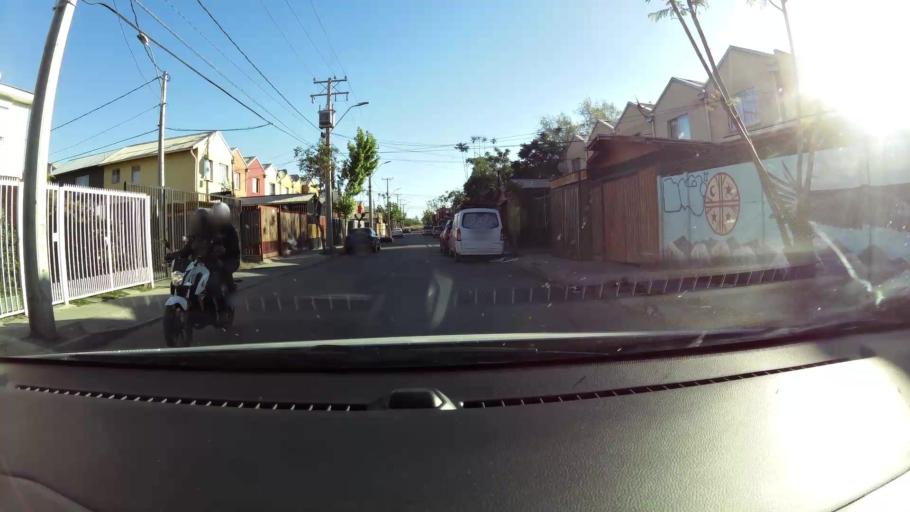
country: CL
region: Santiago Metropolitan
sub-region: Provincia de Maipo
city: San Bernardo
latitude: -33.6031
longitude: -70.6752
